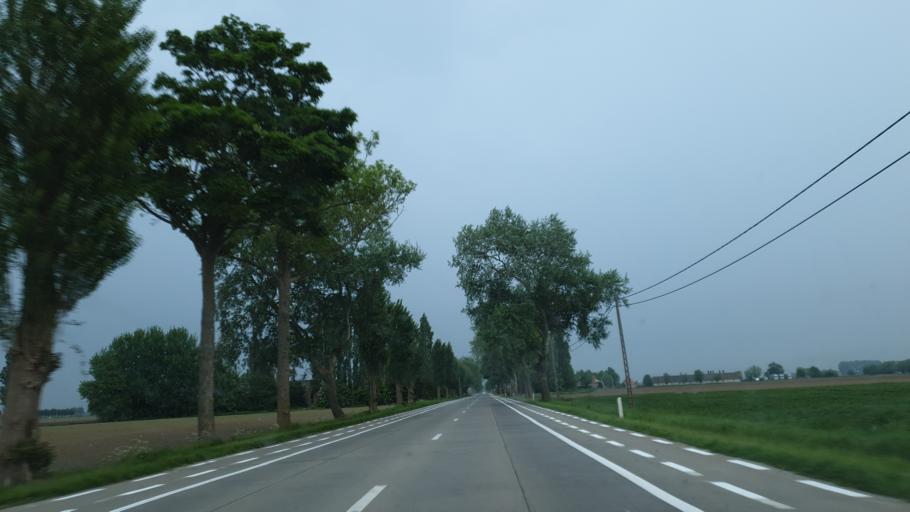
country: BE
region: Flanders
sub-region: Provincie West-Vlaanderen
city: Poperinge
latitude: 50.9282
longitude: 2.7427
